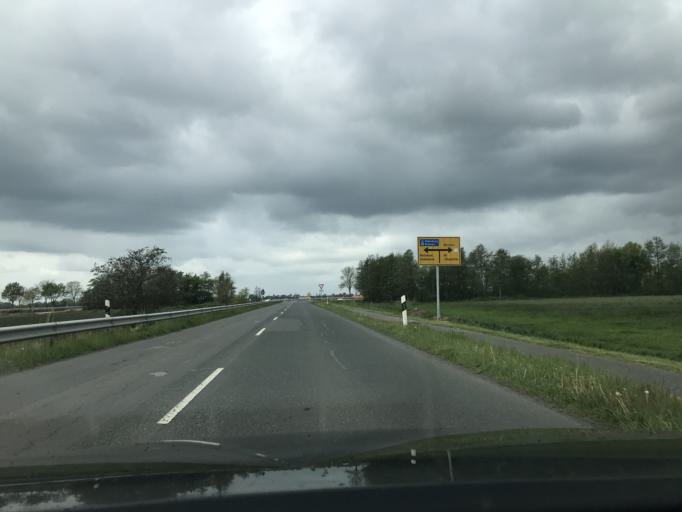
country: DE
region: Lower Saxony
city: Lemwerder
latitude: 53.1564
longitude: 8.5609
